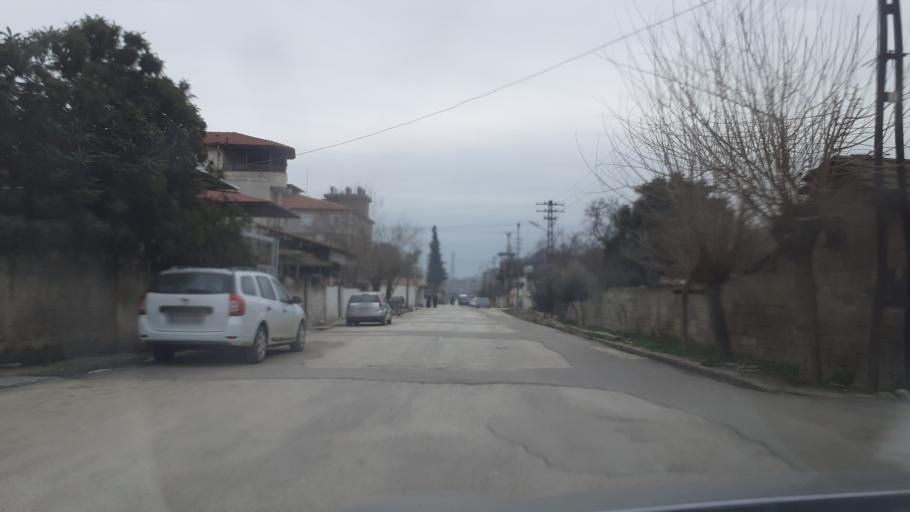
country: TR
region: Hatay
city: Kirikhan
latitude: 36.4889
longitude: 36.3557
